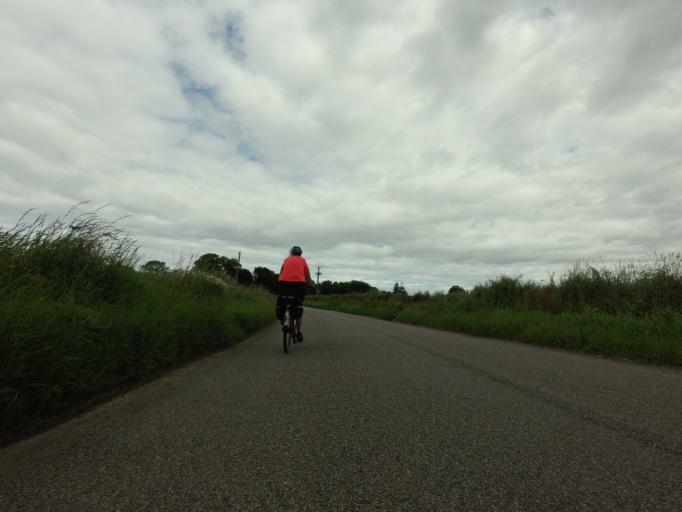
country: GB
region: Scotland
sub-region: Moray
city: Forres
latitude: 57.6155
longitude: -3.6533
